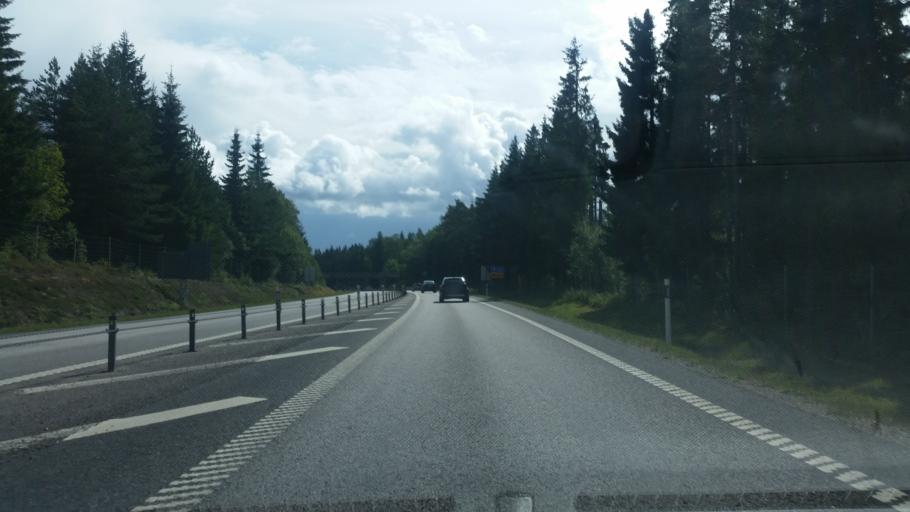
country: SE
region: Joenkoeping
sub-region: Mullsjo Kommun
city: Mullsjoe
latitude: 57.7660
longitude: 13.7246
